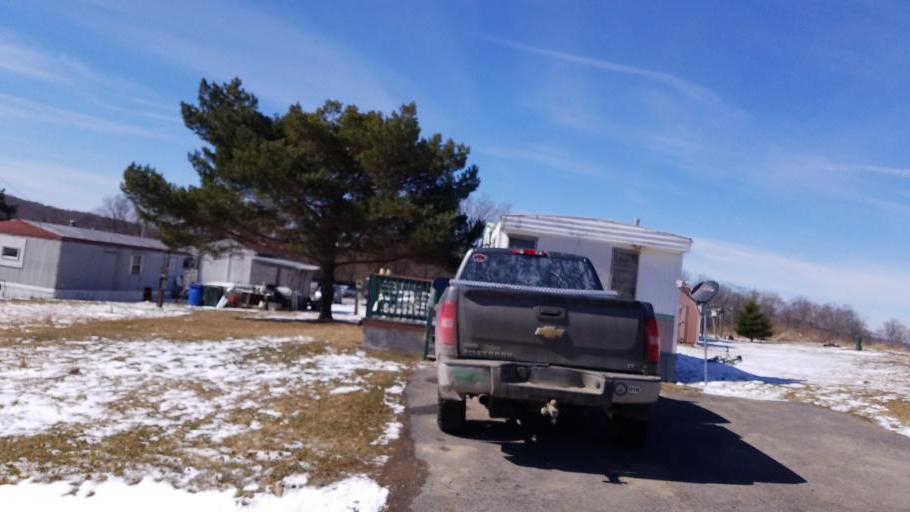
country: US
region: Pennsylvania
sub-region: Potter County
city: Galeton
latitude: 41.9009
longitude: -77.7542
